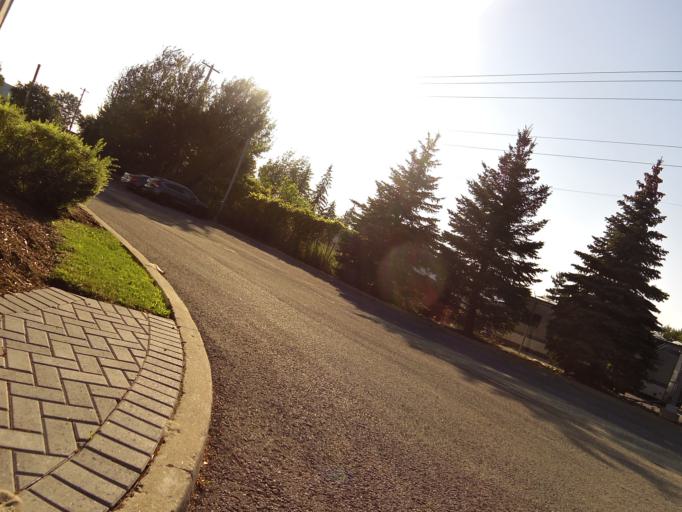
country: CA
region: Ontario
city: Ottawa
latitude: 45.3365
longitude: -75.7019
